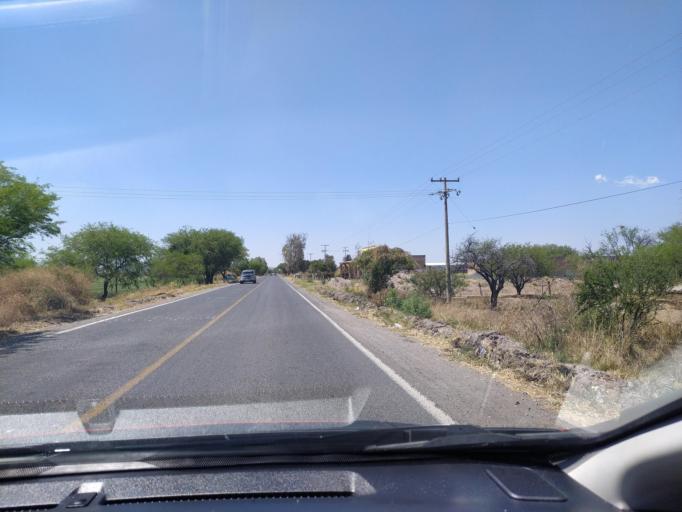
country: MX
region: Guanajuato
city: Ciudad Manuel Doblado
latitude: 20.7421
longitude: -101.8878
